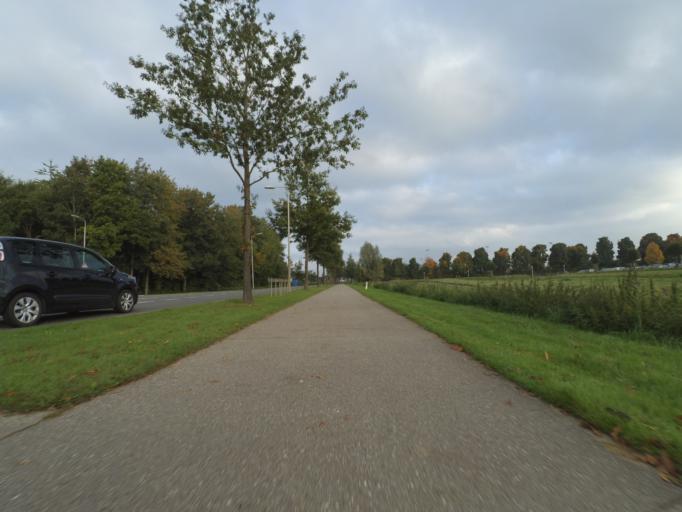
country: NL
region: Flevoland
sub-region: Gemeente Dronten
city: Dronten
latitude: 52.5293
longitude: 5.6938
